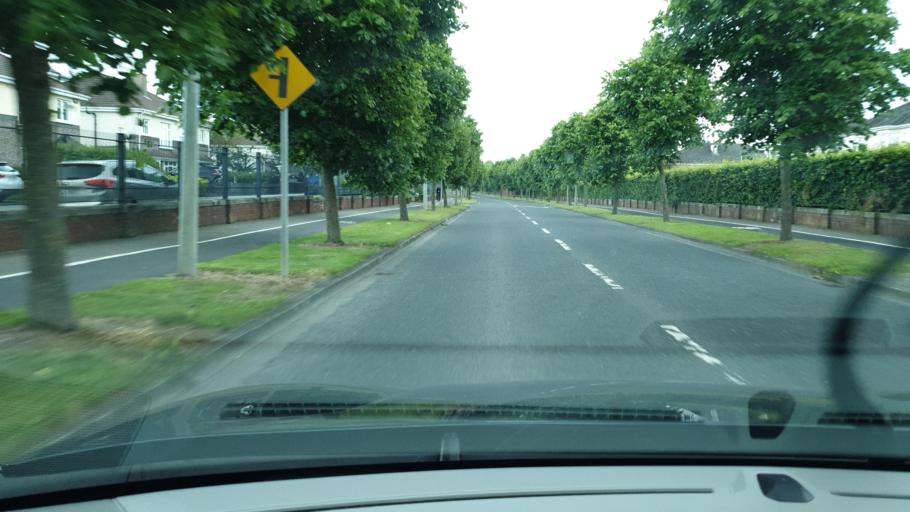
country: IE
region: Leinster
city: Lucan
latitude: 53.3414
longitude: -6.4453
